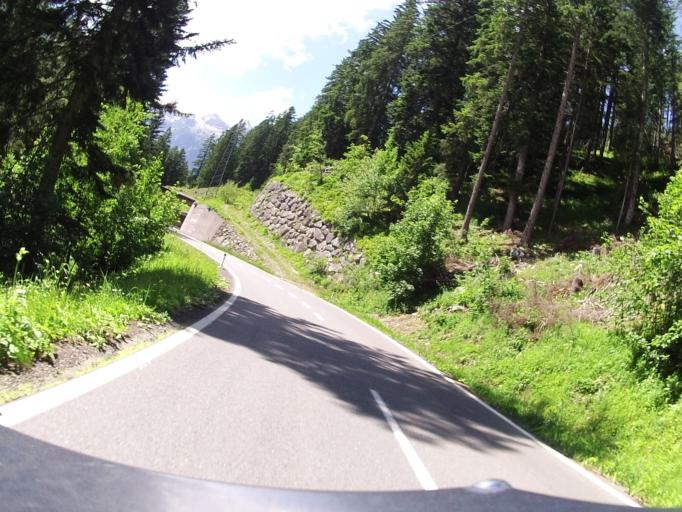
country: AT
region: Tyrol
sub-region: Politischer Bezirk Reutte
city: Elmen
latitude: 47.3167
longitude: 10.5576
